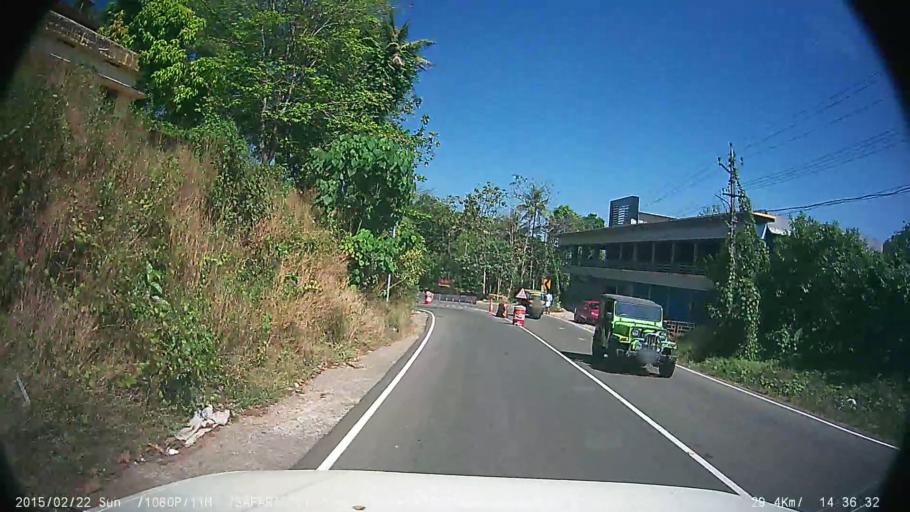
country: IN
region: Kerala
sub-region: Kottayam
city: Erattupetta
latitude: 9.5537
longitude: 76.7890
